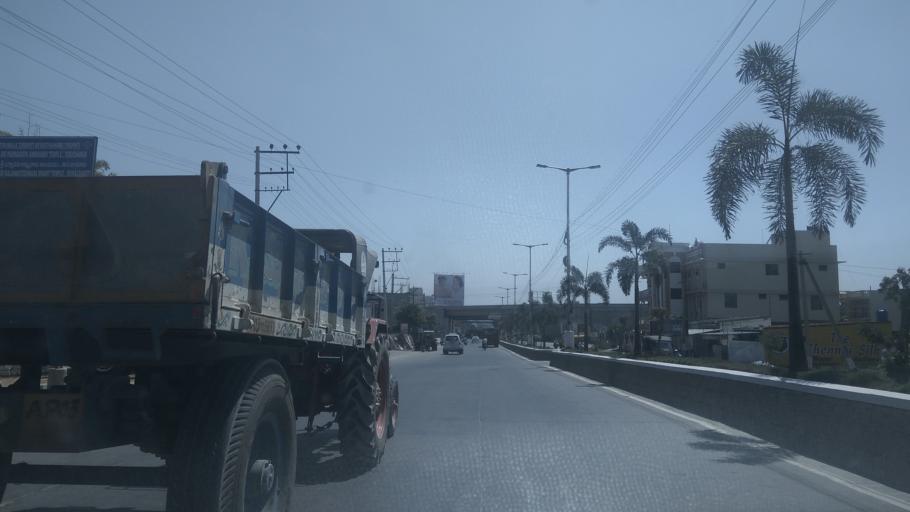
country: IN
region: Andhra Pradesh
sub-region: Chittoor
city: Tirupati
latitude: 13.6120
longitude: 79.4410
